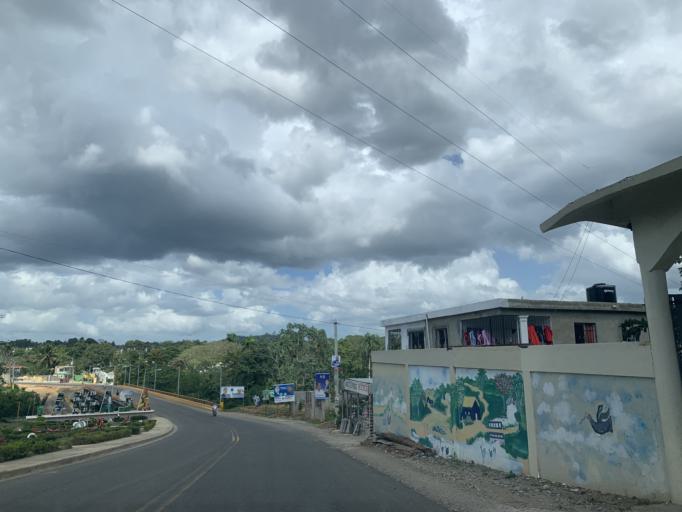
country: DO
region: Monte Plata
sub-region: Yamasa
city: Yamasa
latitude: 18.7625
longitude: -70.0192
